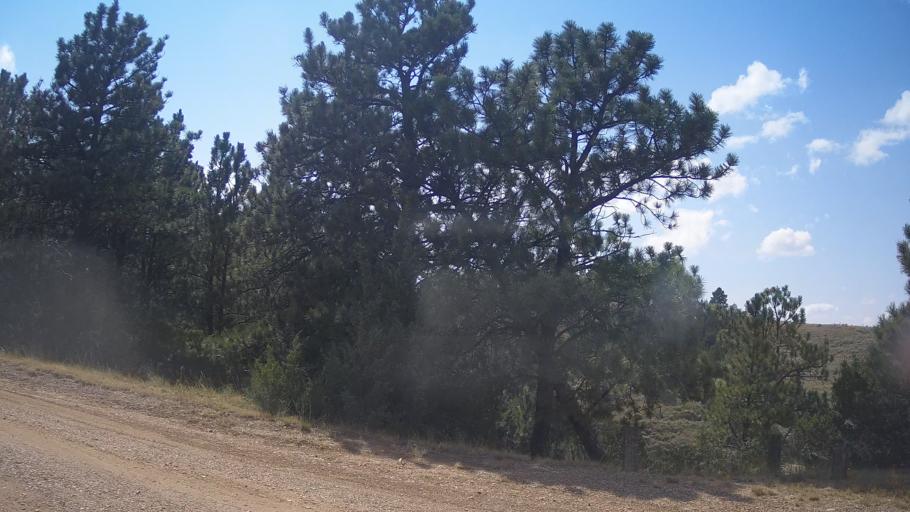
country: US
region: Montana
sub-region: Dawson County
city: Glendive
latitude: 47.0584
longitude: -104.6637
